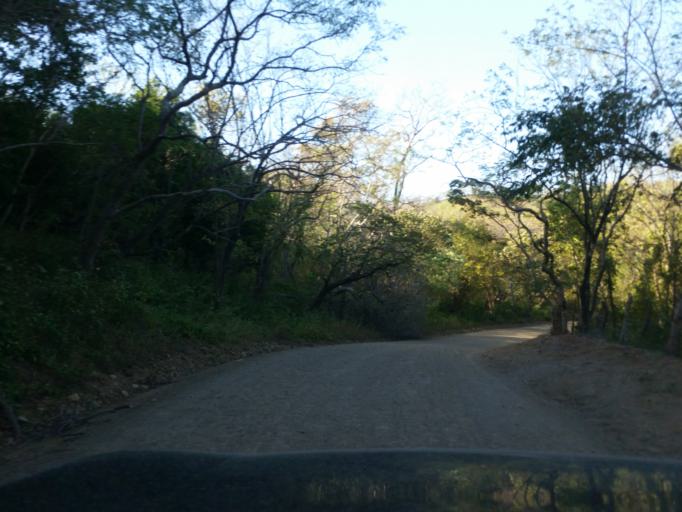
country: NI
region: Rivas
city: San Juan del Sur
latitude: 11.2151
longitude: -85.8121
